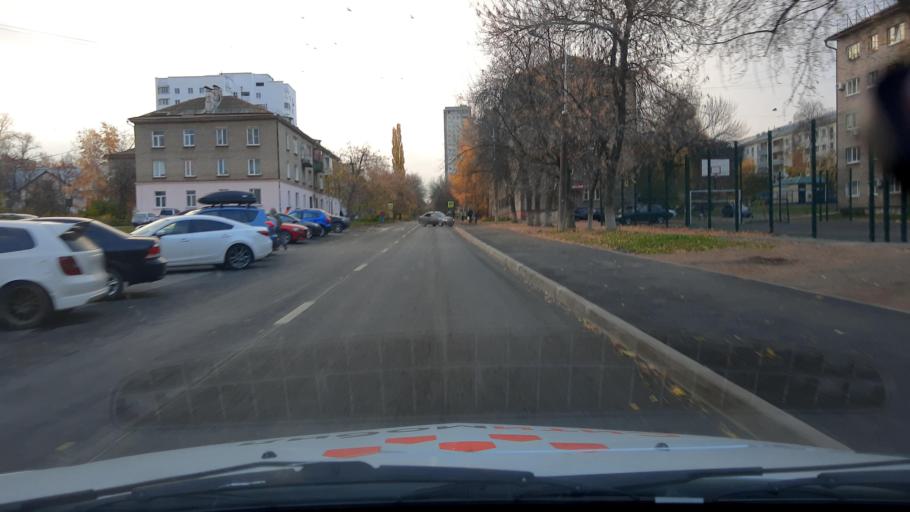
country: RU
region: Bashkortostan
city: Ufa
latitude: 54.7893
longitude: 56.0378
